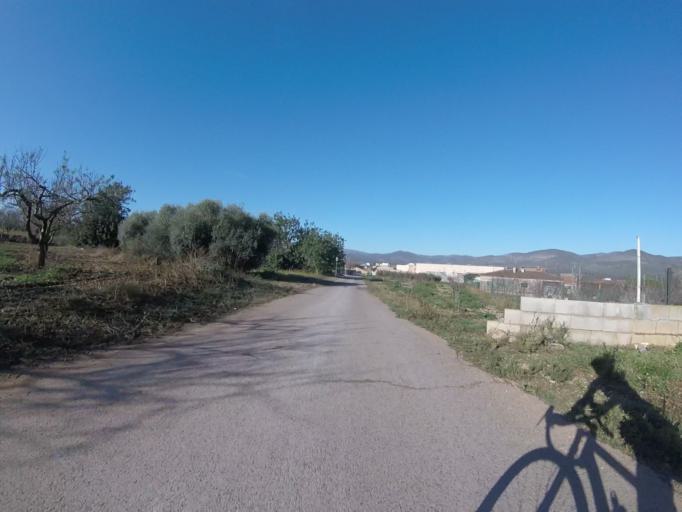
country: ES
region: Valencia
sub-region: Provincia de Castello
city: Santa Magdalena de Pulpis
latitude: 40.3556
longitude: 0.3060
